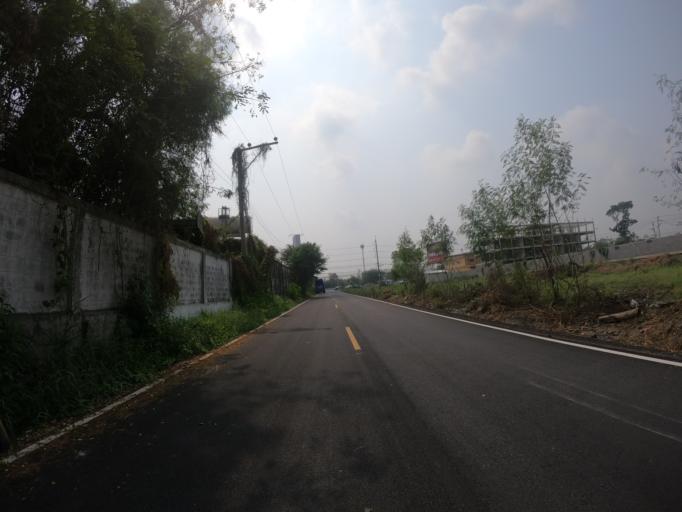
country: TH
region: Pathum Thani
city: Nong Suea
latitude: 14.0625
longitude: 100.8491
